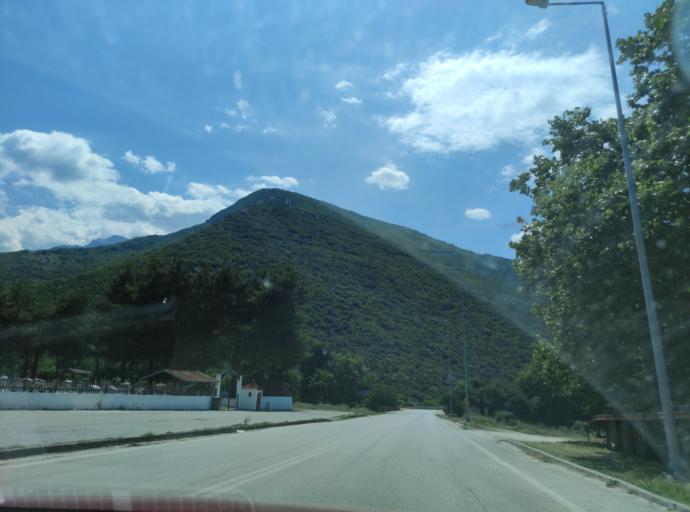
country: GR
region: East Macedonia and Thrace
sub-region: Nomos Kavalas
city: Nikisiani
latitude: 40.9729
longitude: 24.1402
